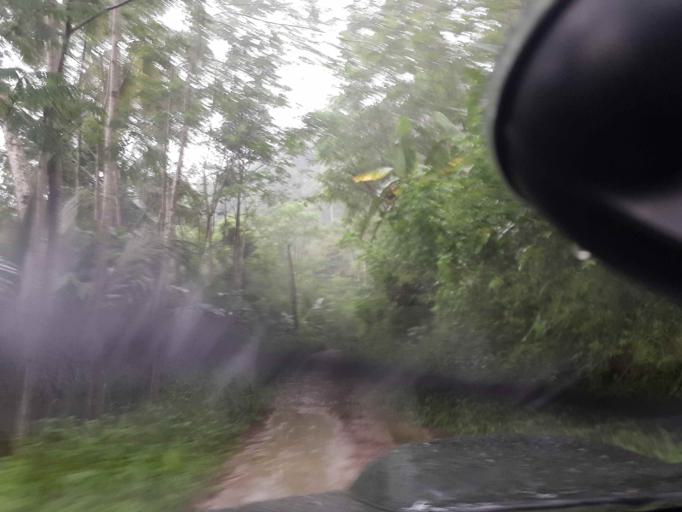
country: ID
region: Central Java
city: Wonosobo
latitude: -7.4942
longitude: 109.9603
